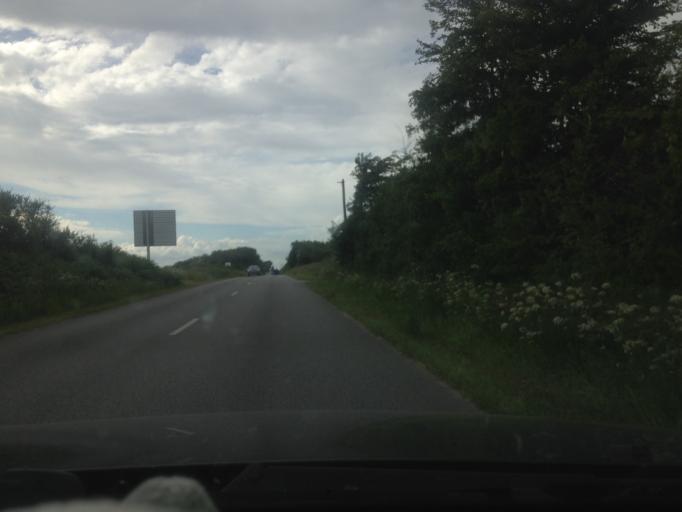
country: FR
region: Brittany
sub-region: Departement du Morbihan
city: Erdeven
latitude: 47.6222
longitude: -3.1369
